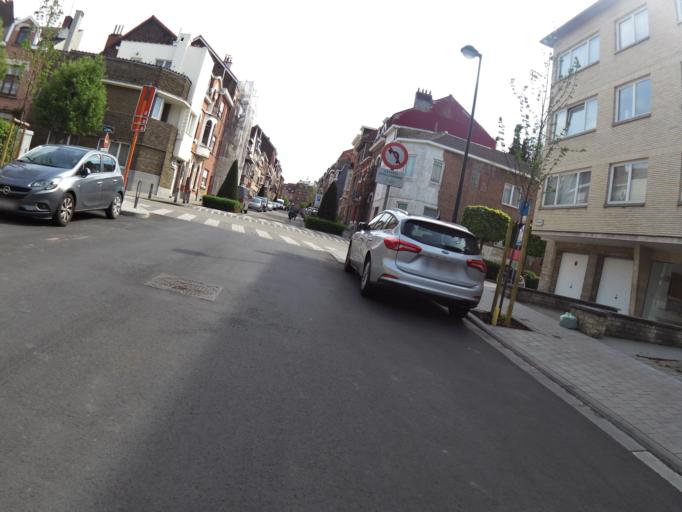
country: BE
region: Flanders
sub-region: Provincie Vlaams-Brabant
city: Kraainem
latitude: 50.8387
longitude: 4.4182
